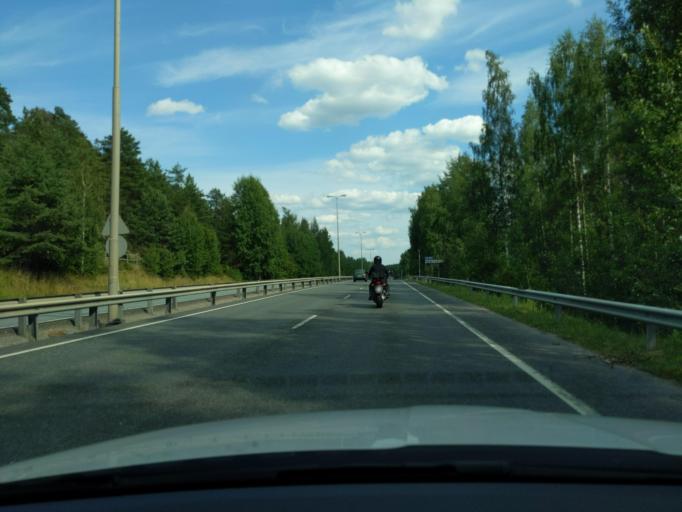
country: FI
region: Paijanne Tavastia
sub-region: Lahti
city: Lahti
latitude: 60.9758
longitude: 25.6859
